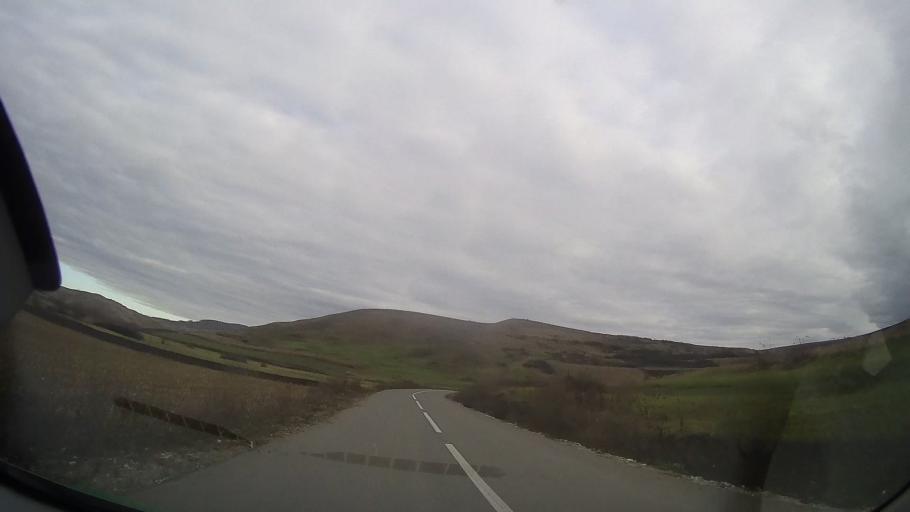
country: RO
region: Bistrita-Nasaud
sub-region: Comuna Silvasu de Campie
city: Silvasu de Campie
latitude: 46.7937
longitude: 24.2929
